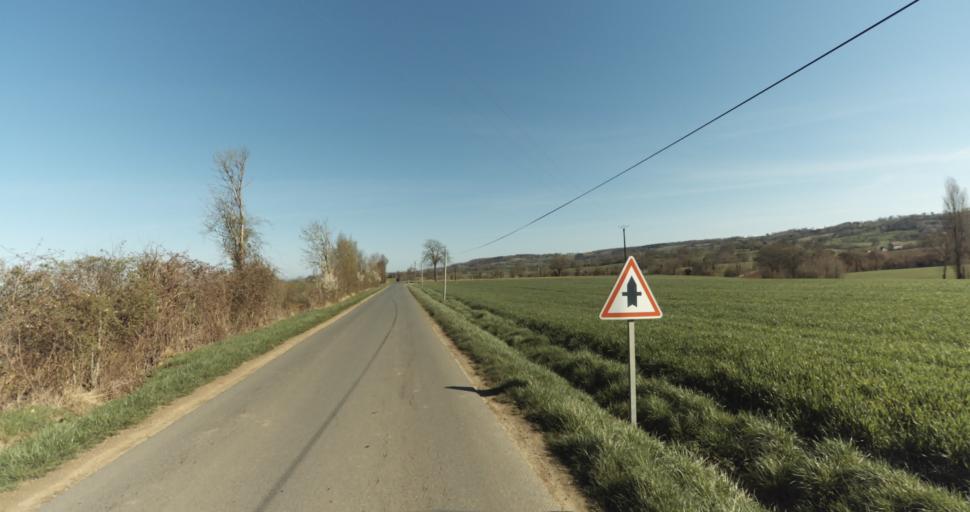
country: FR
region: Lower Normandy
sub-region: Departement de l'Orne
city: Trun
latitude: 48.9048
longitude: 0.0337
